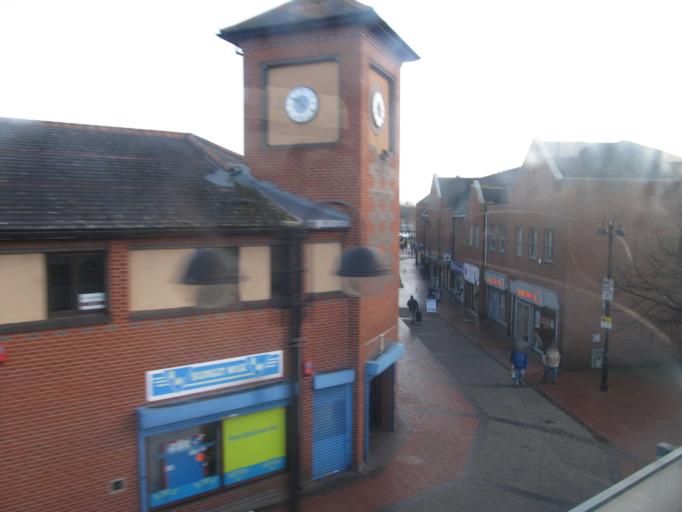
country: GB
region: England
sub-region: Nottinghamshire
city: Hucknall
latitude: 53.0021
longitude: -1.1976
